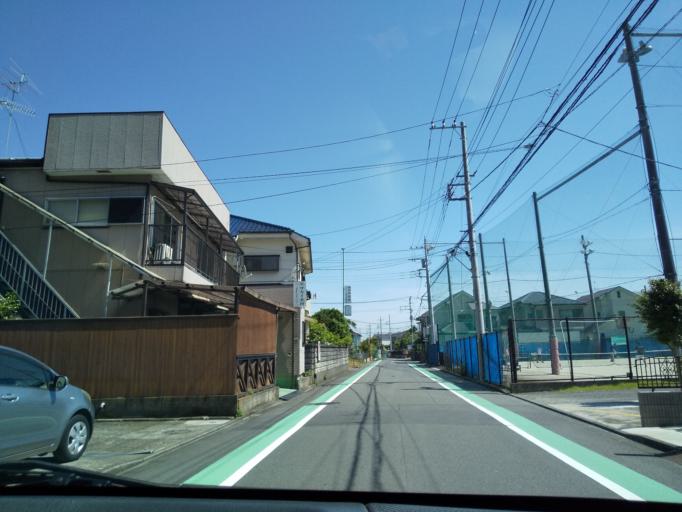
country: JP
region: Kanagawa
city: Zama
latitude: 35.5490
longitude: 139.3667
